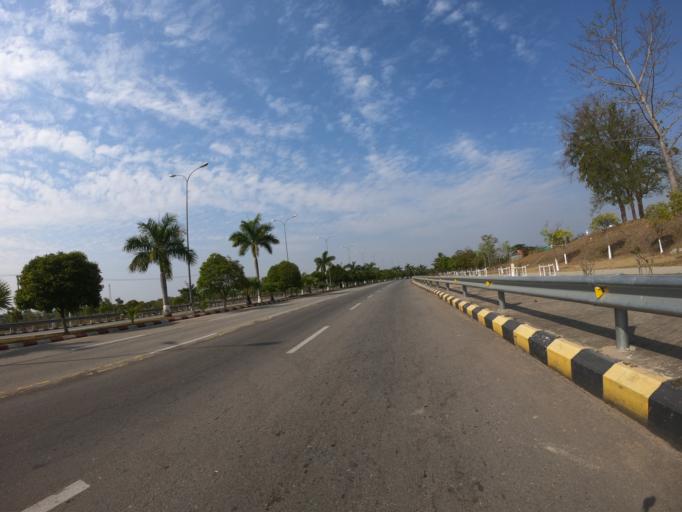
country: MM
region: Mandalay
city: Nay Pyi Taw
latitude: 19.6669
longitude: 96.1208
